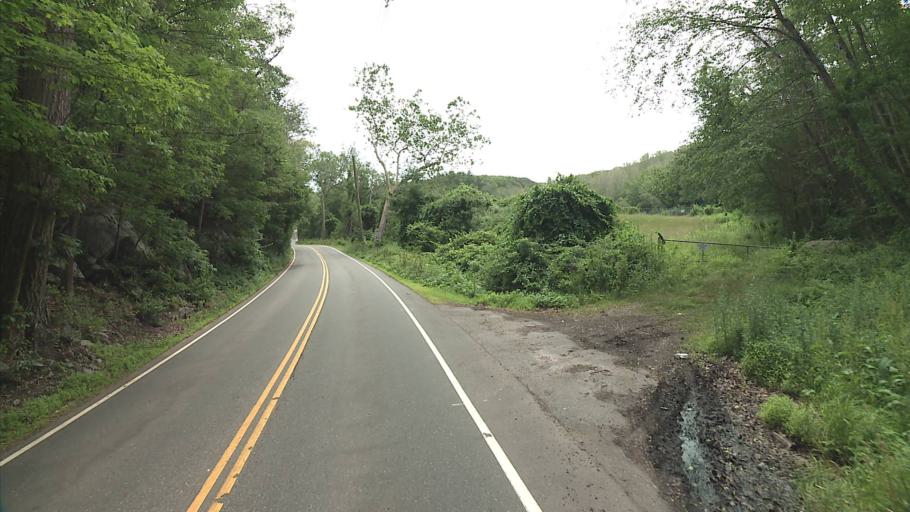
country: US
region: Connecticut
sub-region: New London County
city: Gales Ferry
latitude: 41.4522
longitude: -72.0586
